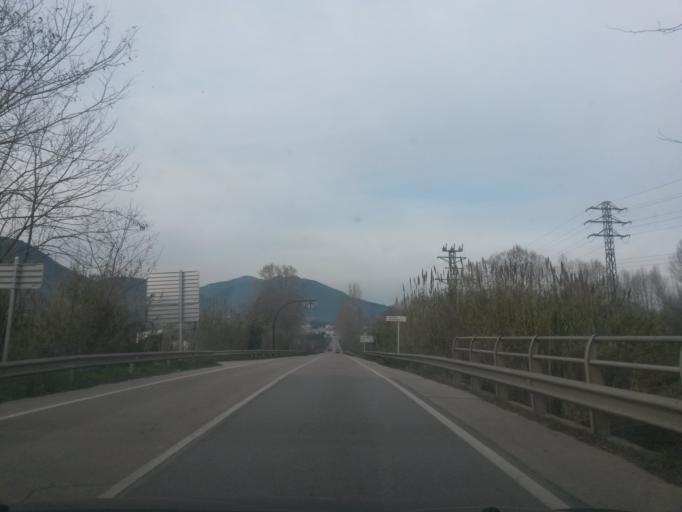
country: ES
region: Catalonia
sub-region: Provincia de Girona
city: Angles
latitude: 41.9620
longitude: 2.6306
